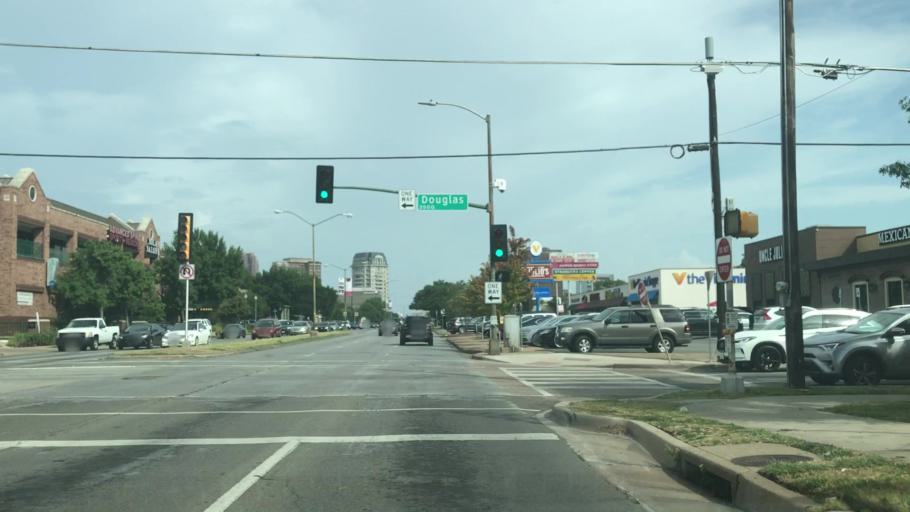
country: US
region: Texas
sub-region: Dallas County
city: Highland Park
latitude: 32.8158
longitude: -96.8103
